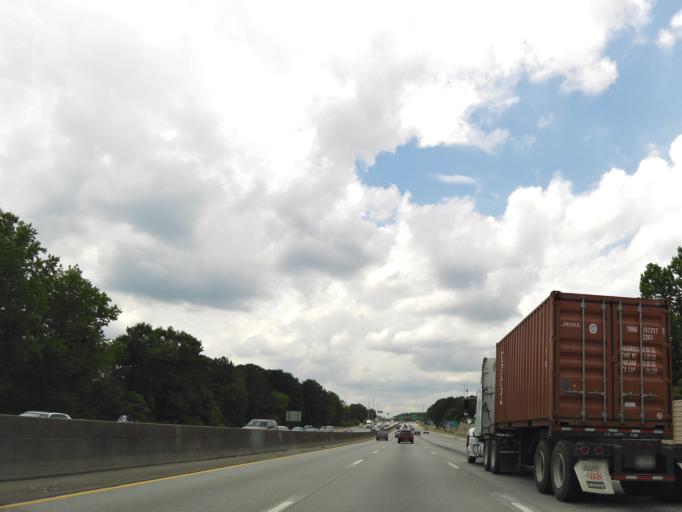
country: US
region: Georgia
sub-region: Clayton County
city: Morrow
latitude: 33.5691
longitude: -84.3262
